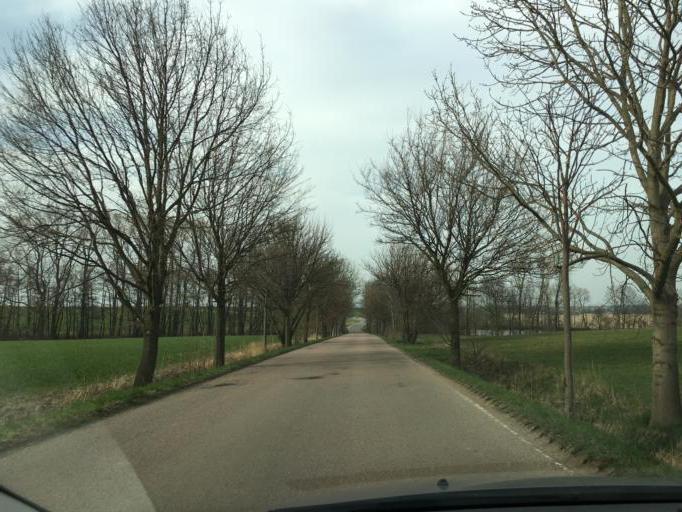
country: DE
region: Saxony
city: Niederfrohna
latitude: 50.8806
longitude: 12.7100
